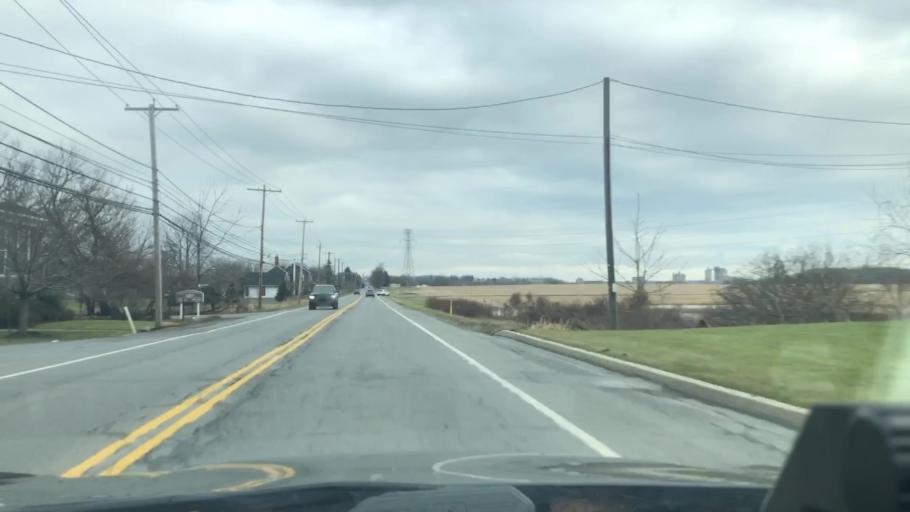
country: US
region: Pennsylvania
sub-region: Northampton County
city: Nazareth
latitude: 40.7154
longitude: -75.3228
